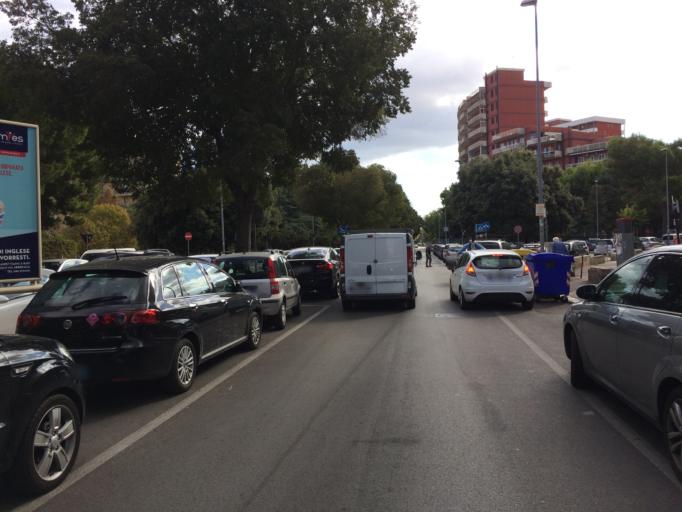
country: IT
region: Apulia
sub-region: Provincia di Bari
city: Bari
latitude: 41.0931
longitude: 16.8606
